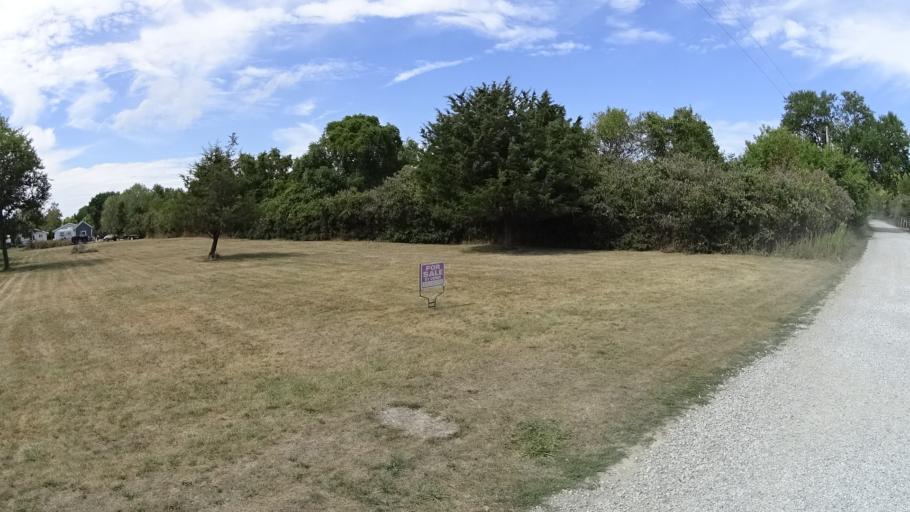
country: US
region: Ohio
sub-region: Erie County
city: Sandusky
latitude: 41.5923
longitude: -82.6860
